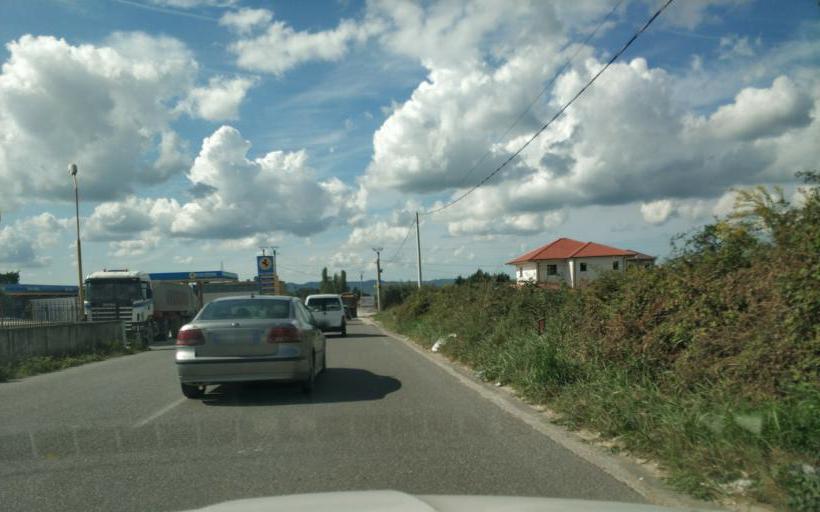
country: AL
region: Durres
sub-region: Rrethi i Krujes
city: Nikel
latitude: 41.4783
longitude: 19.7532
